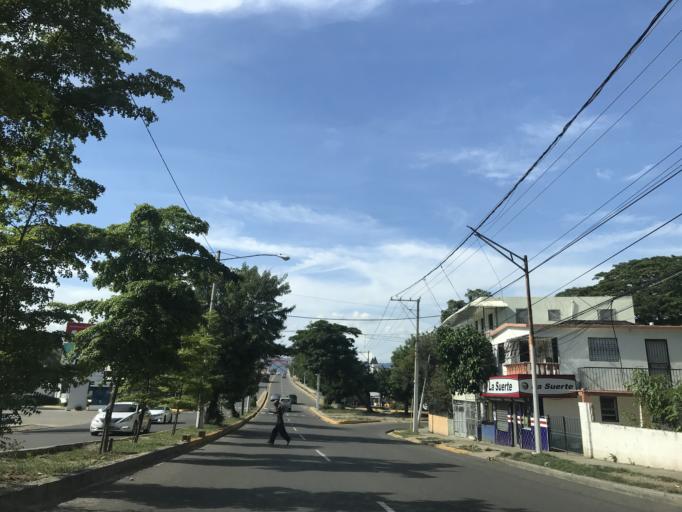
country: DO
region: Santiago
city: Santiago de los Caballeros
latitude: 19.4443
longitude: -70.7094
